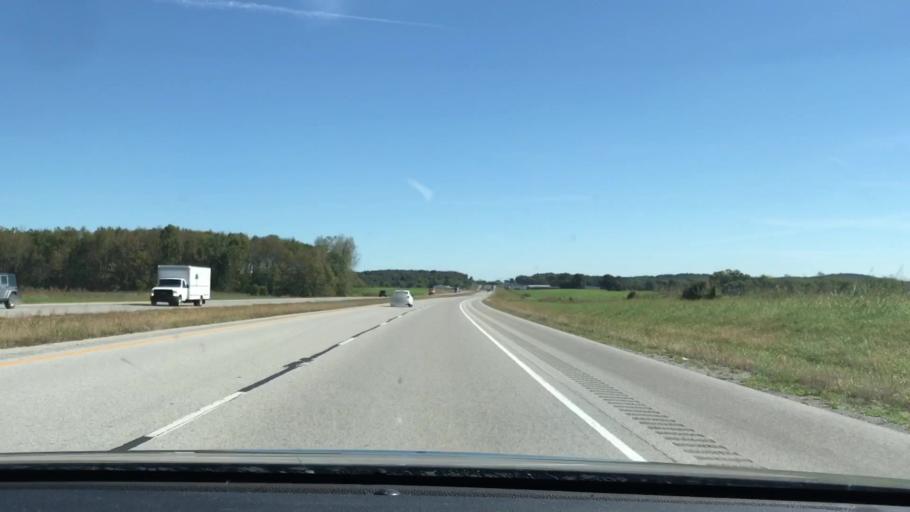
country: US
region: Kentucky
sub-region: Logan County
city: Auburn
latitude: 36.8532
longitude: -86.7645
